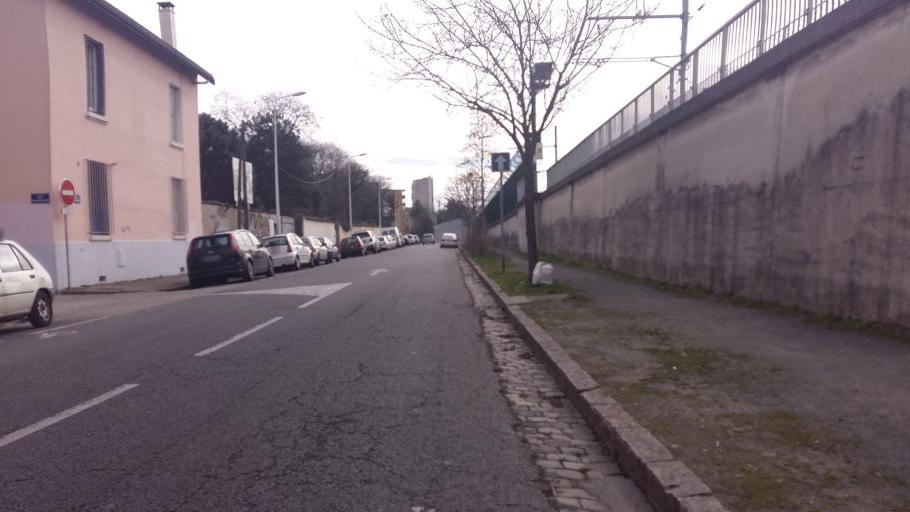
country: FR
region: Rhone-Alpes
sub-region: Departement du Rhone
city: Lyon
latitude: 45.7344
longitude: 4.8504
